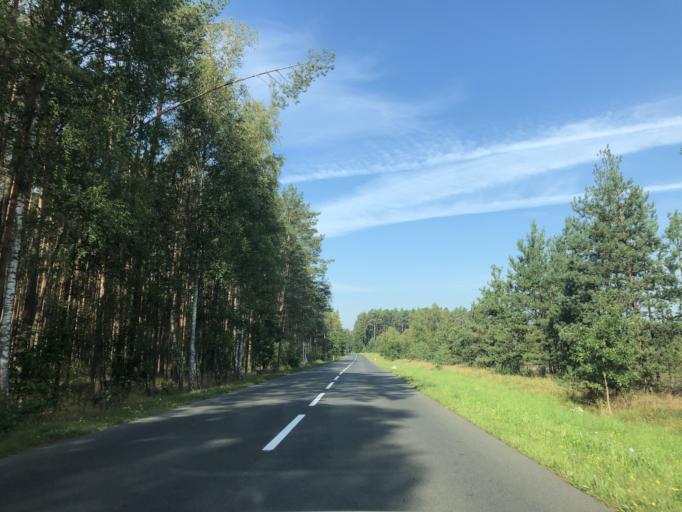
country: PL
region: Greater Poland Voivodeship
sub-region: Powiat pilski
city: Kaczory
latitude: 53.1208
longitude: 16.8202
